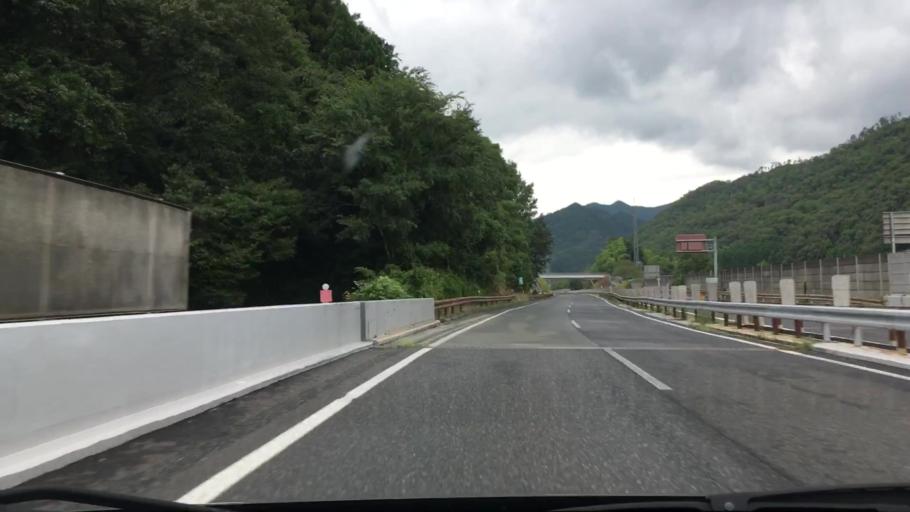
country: JP
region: Okayama
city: Niimi
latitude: 35.0013
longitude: 133.4435
